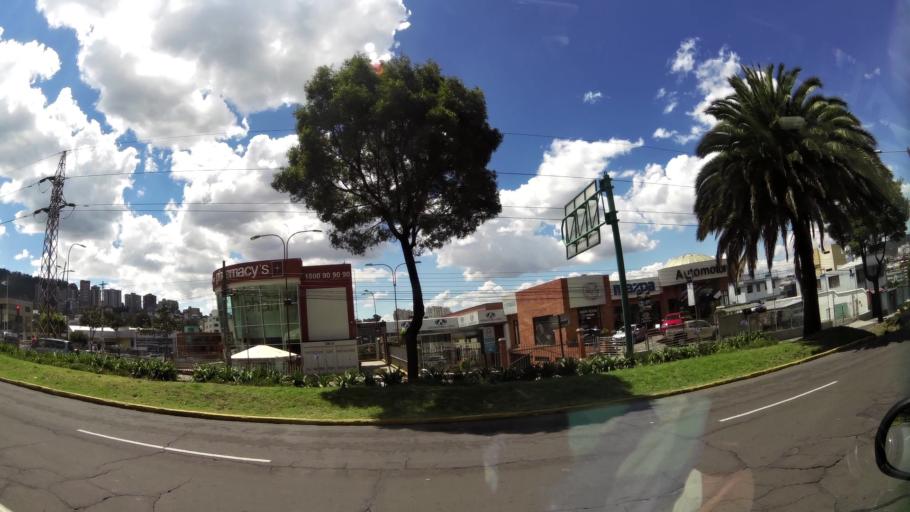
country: EC
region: Pichincha
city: Quito
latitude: -0.1746
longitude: -78.4926
